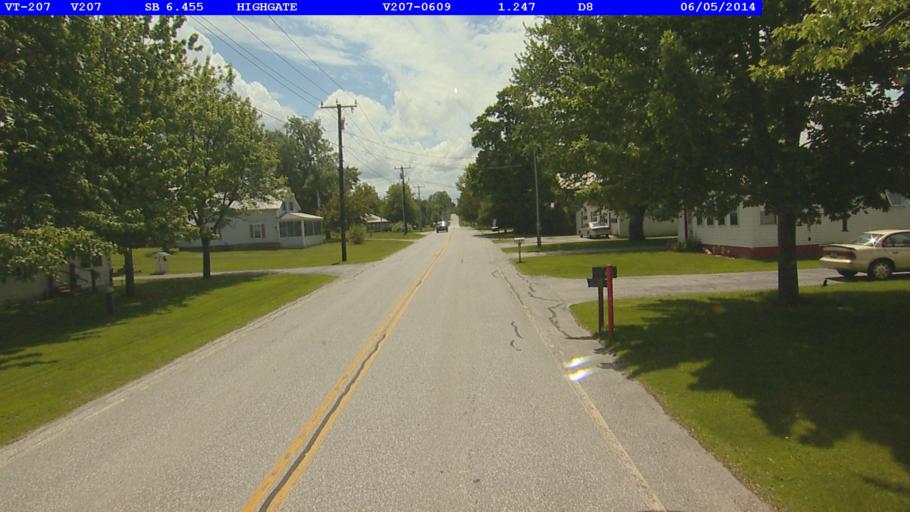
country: US
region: Vermont
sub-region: Franklin County
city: Swanton
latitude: 44.9285
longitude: -73.0499
